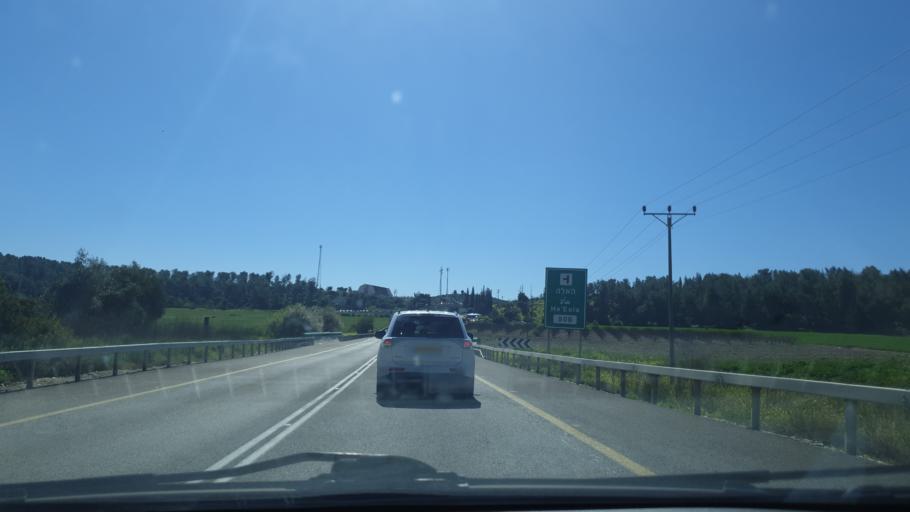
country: IL
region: Jerusalem
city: Bet Shemesh
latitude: 31.6916
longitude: 34.9436
